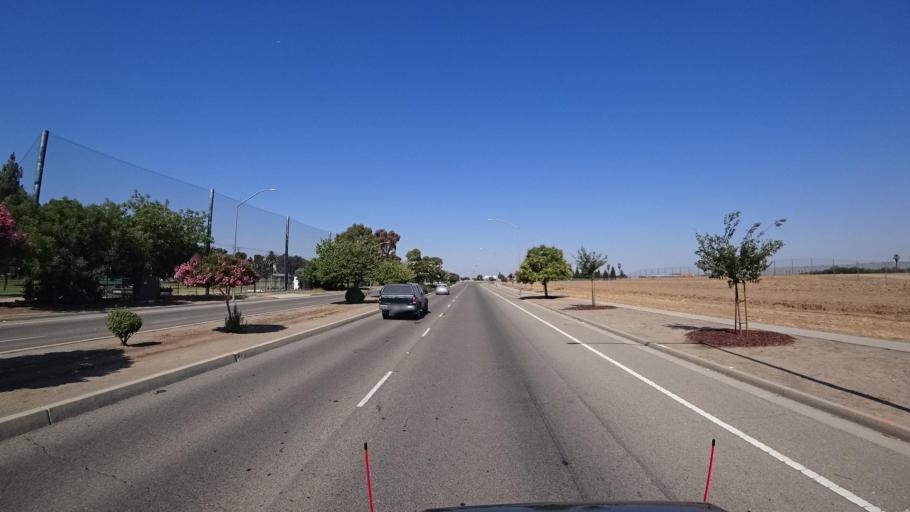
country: US
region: California
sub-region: Fresno County
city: Tarpey Village
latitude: 36.7795
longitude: -119.7066
